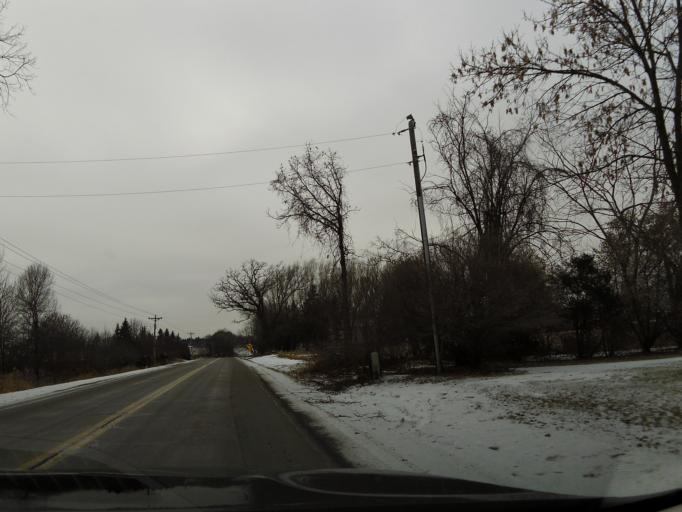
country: US
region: Minnesota
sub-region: Hennepin County
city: Medina
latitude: 45.0401
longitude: -93.5731
